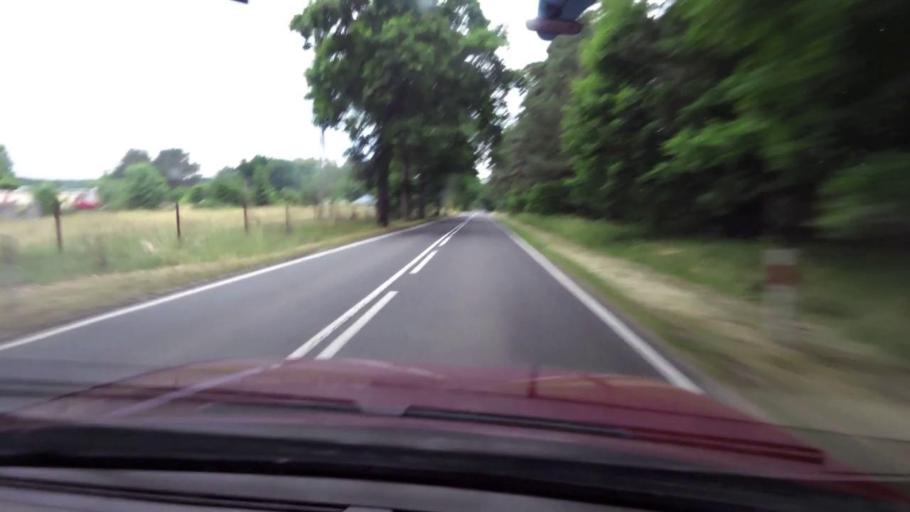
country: PL
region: West Pomeranian Voivodeship
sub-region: Powiat koszalinski
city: Sianow
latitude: 54.1818
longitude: 16.3265
